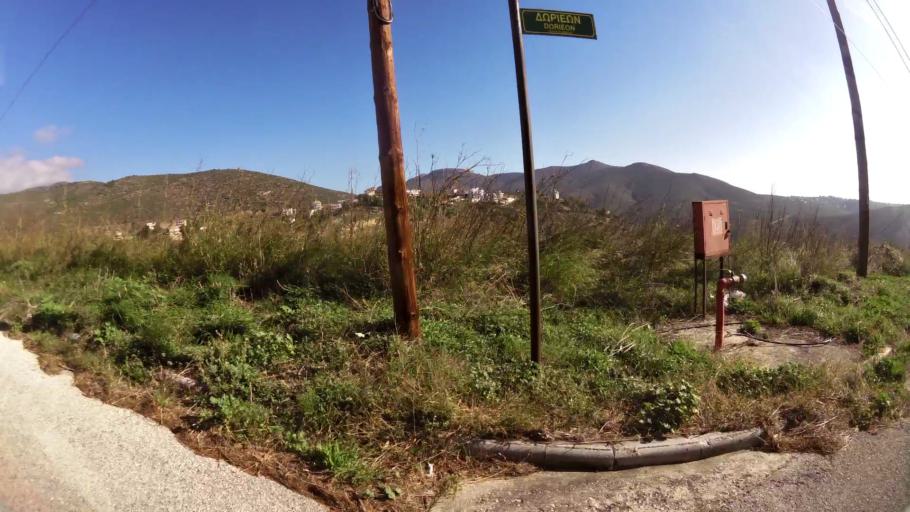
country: GR
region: Attica
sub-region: Nomarchia Anatolikis Attikis
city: Dhrafi
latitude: 38.0397
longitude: 23.8967
